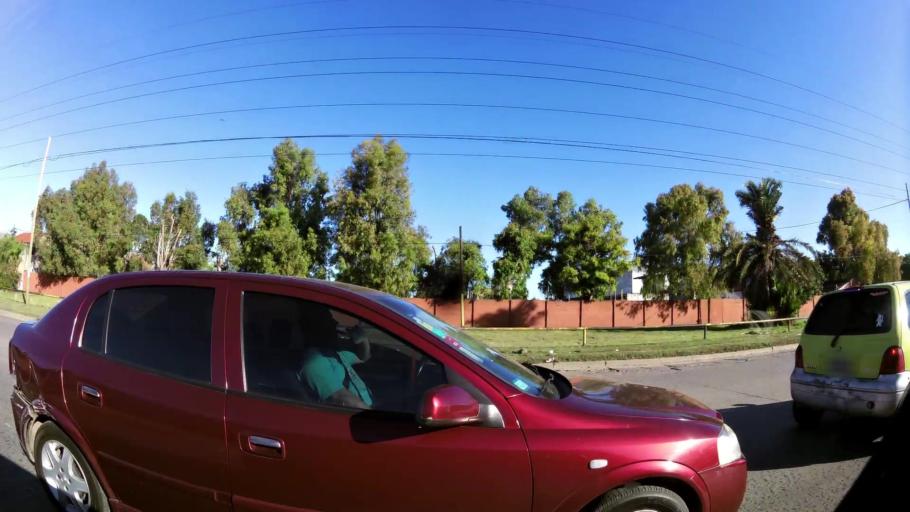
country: AR
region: Buenos Aires
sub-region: Partido de Quilmes
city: Quilmes
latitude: -34.7427
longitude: -58.3248
